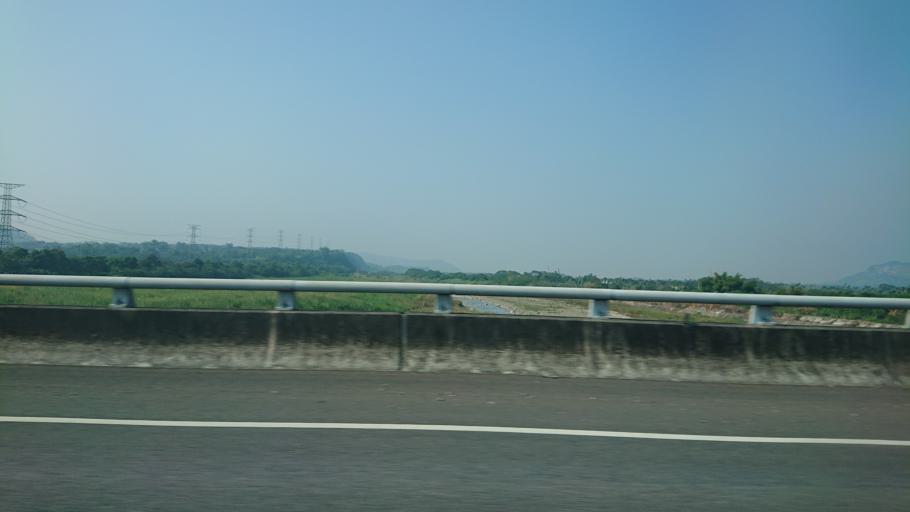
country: TW
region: Taiwan
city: Lugu
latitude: 23.7916
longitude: 120.7037
